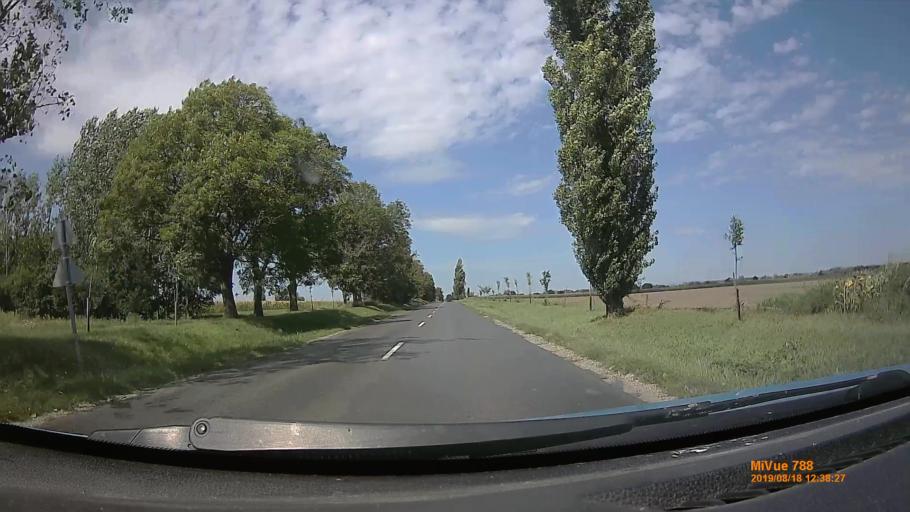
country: HU
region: Fejer
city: Szabadbattyan
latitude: 47.0889
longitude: 18.3987
